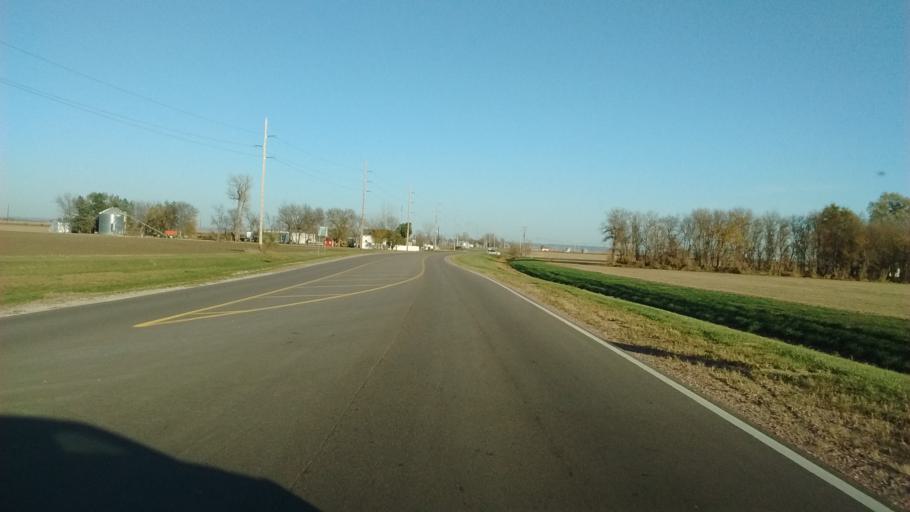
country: US
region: Iowa
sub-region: Woodbury County
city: Sergeant Bluff
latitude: 42.3300
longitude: -96.3138
